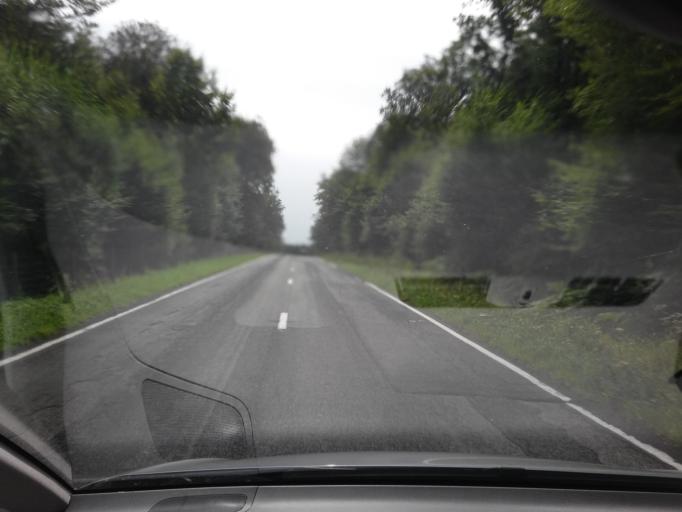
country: BE
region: Wallonia
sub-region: Province du Luxembourg
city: Chiny
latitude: 49.7730
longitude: 5.3555
